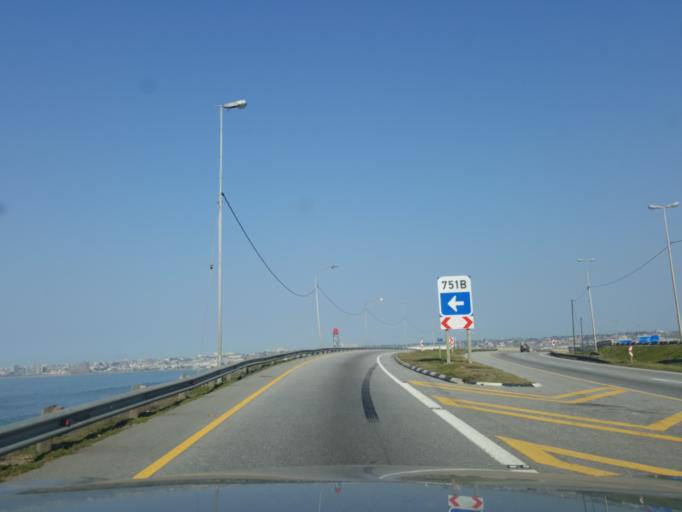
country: ZA
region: Eastern Cape
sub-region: Nelson Mandela Bay Metropolitan Municipality
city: Port Elizabeth
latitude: -33.9123
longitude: 25.6157
